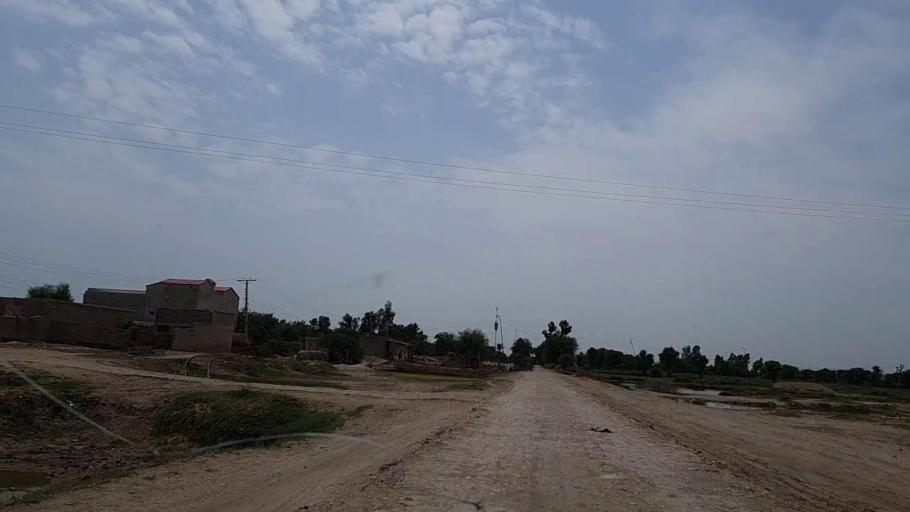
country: PK
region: Sindh
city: Tharu Shah
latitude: 26.9262
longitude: 68.0849
